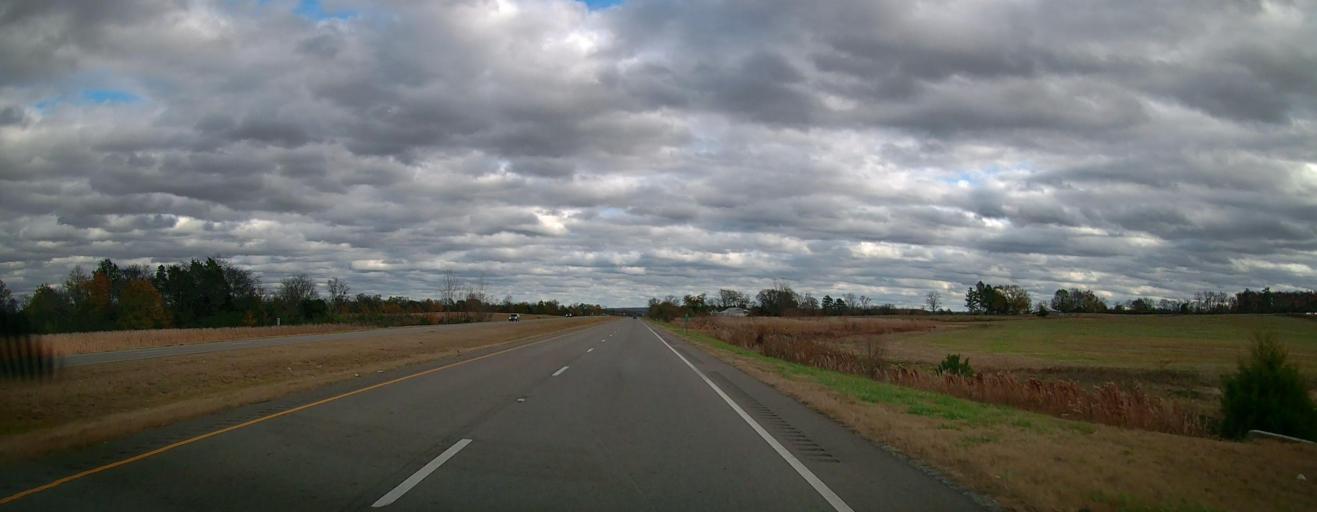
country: US
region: Alabama
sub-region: Morgan County
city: Danville
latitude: 34.3833
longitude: -87.1004
